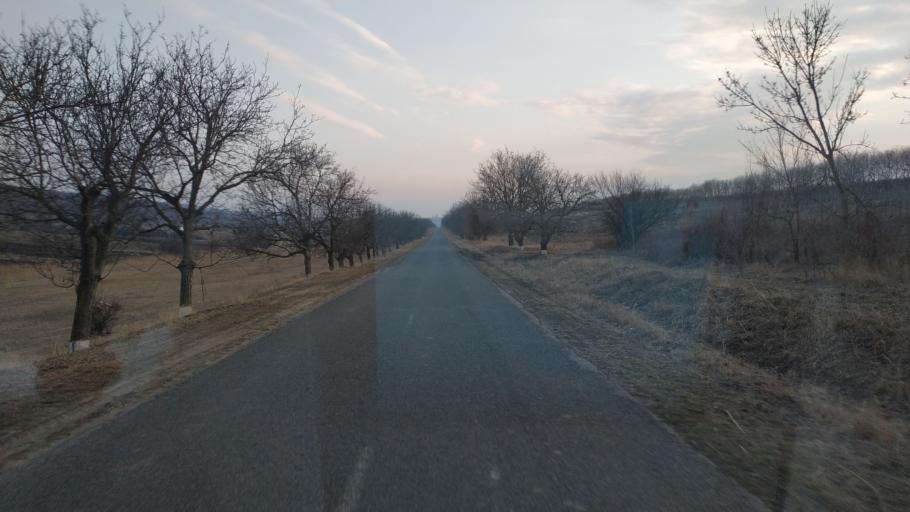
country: MD
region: Hincesti
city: Dancu
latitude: 46.6903
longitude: 28.3360
